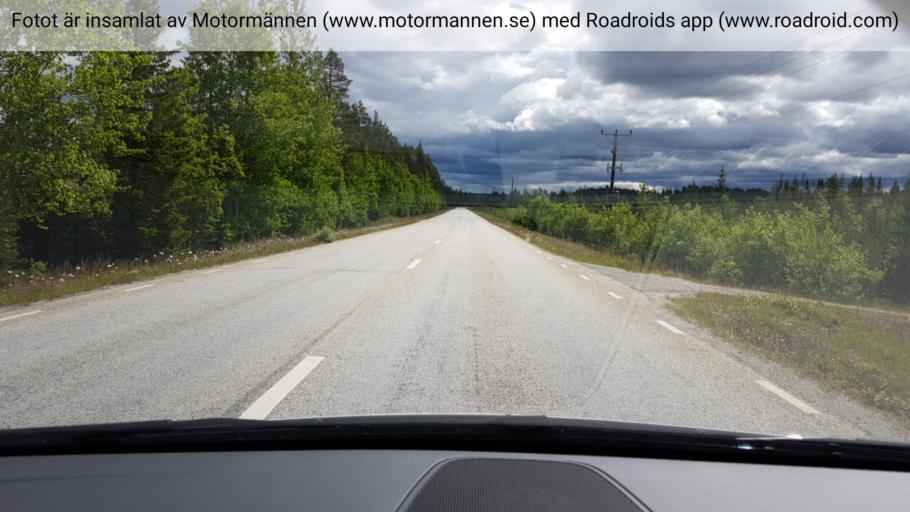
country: SE
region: Jaemtland
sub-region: Bergs Kommun
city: Hoverberg
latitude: 62.4925
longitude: 14.2182
